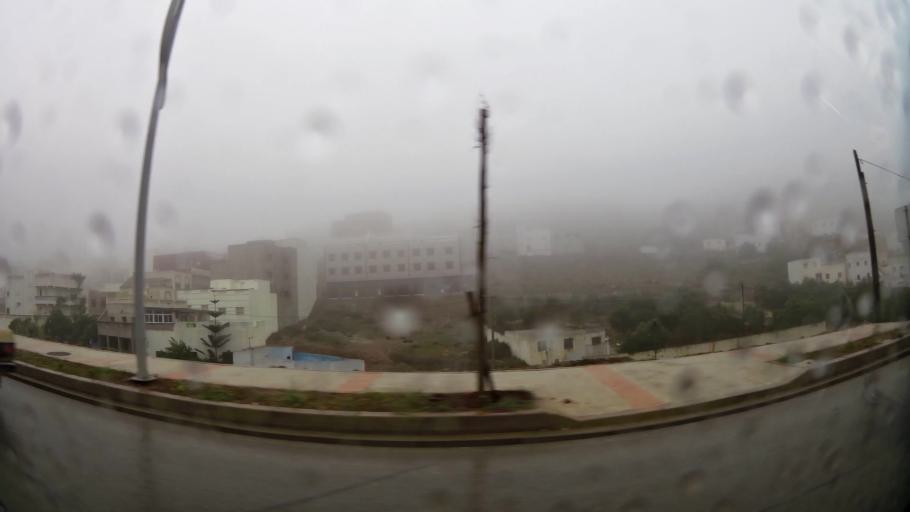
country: MA
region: Taza-Al Hoceima-Taounate
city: Tirhanimine
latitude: 35.2343
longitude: -3.9534
